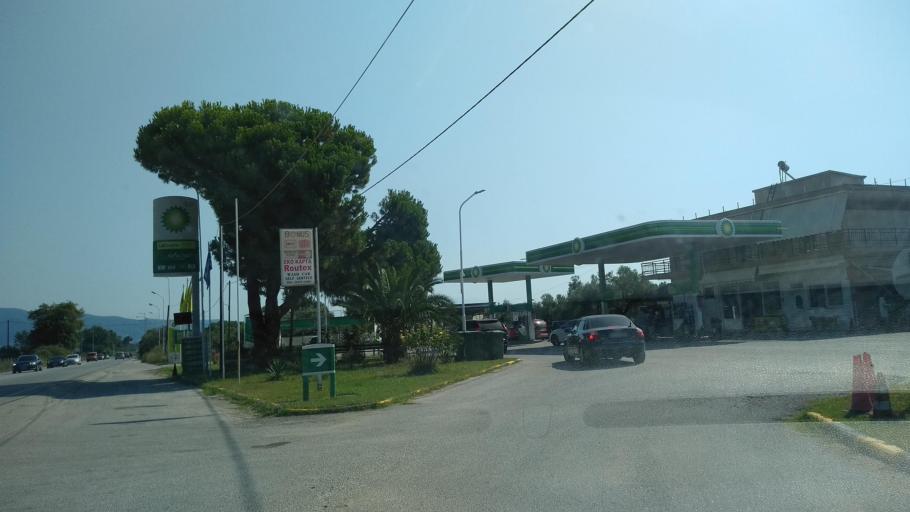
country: GR
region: Central Macedonia
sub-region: Nomos Thessalonikis
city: Nea Vrasna
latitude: 40.7001
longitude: 23.6902
